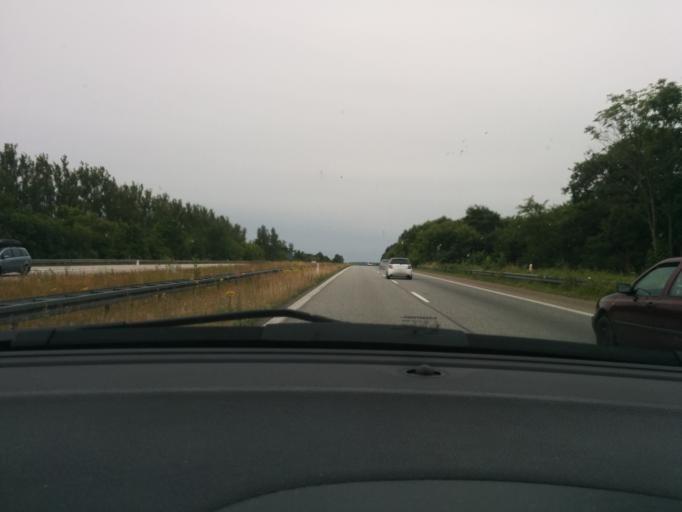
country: DK
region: Zealand
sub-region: Faxe Kommune
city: Ronnede
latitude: 55.3104
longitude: 12.0295
